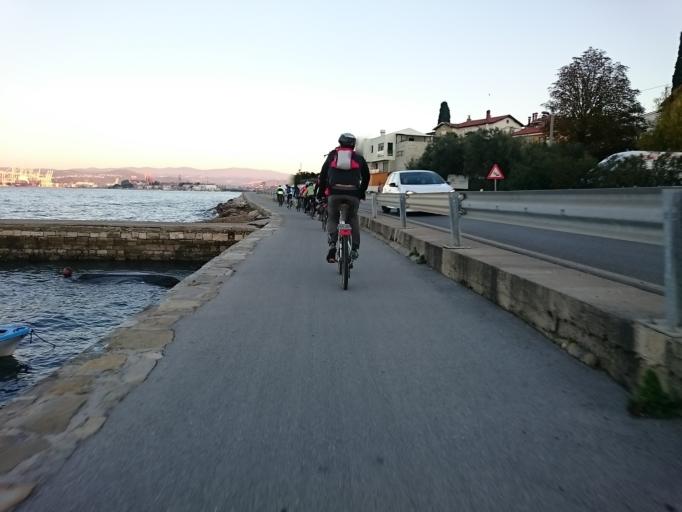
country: SI
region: Koper-Capodistria
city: Koper
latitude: 45.5472
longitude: 13.7051
